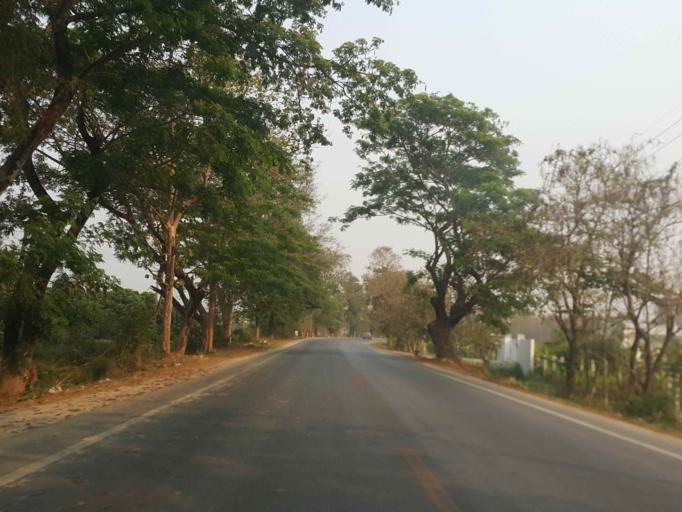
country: TH
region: Chiang Mai
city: Mae Taeng
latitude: 19.0002
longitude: 98.9746
